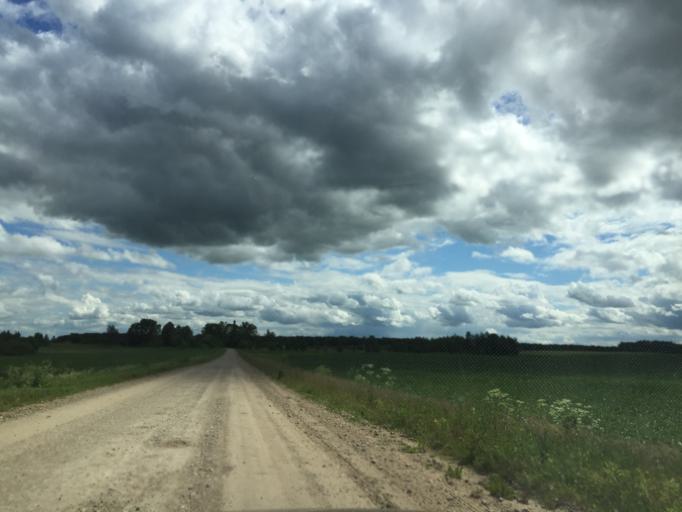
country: LV
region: Vecumnieki
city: Vecumnieki
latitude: 56.4768
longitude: 24.4177
